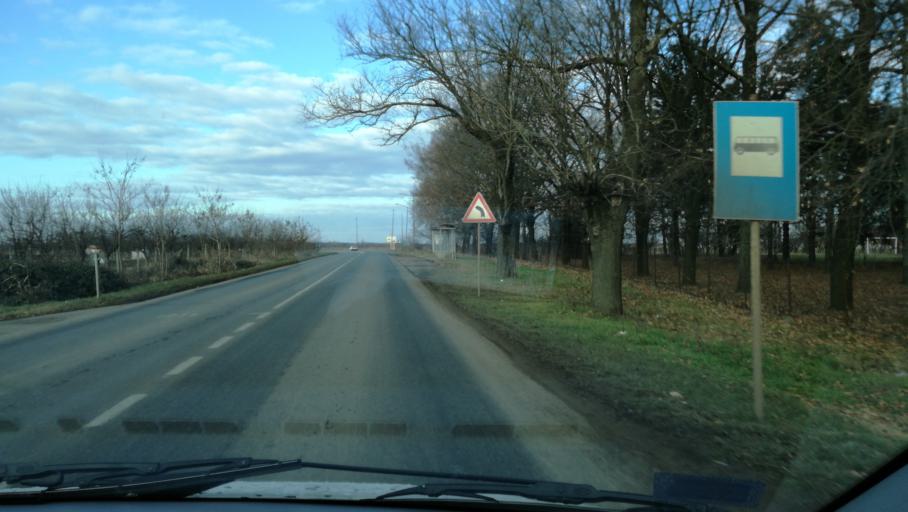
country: RS
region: Autonomna Pokrajina Vojvodina
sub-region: Severnobanatski Okrug
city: Kikinda
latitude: 45.8226
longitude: 20.4309
